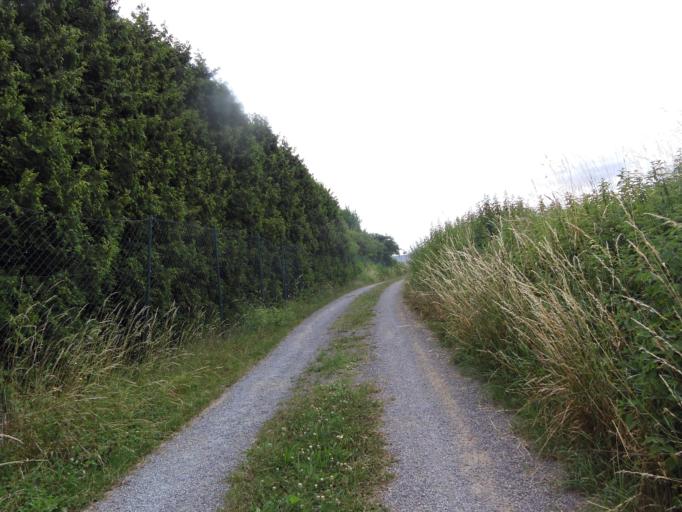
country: DE
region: Bavaria
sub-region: Regierungsbezirk Unterfranken
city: Reichenberg
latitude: 49.7559
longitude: 9.9367
